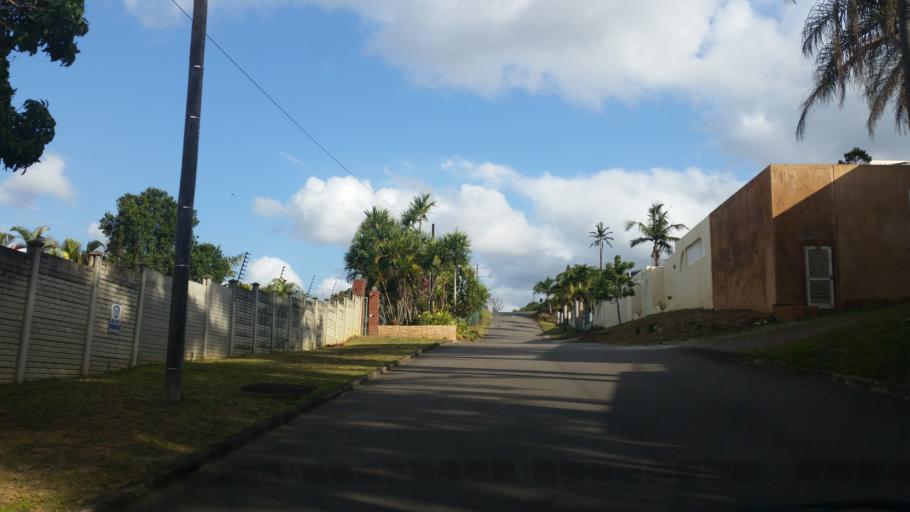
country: ZA
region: KwaZulu-Natal
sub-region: eThekwini Metropolitan Municipality
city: Berea
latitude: -29.8293
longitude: 30.9533
